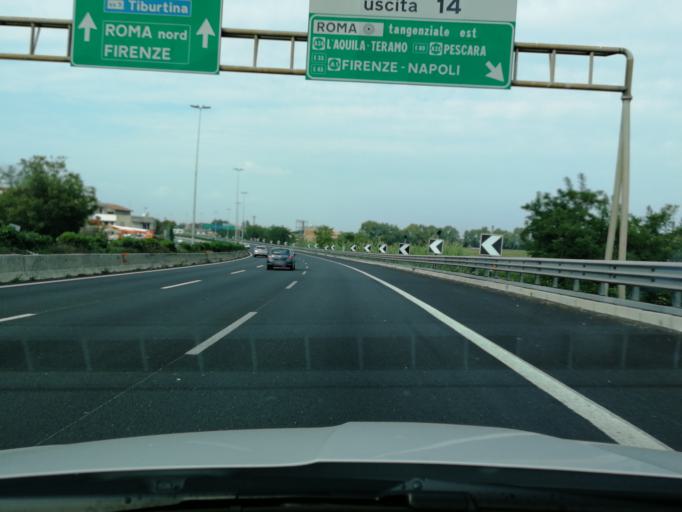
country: IT
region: Latium
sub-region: Citta metropolitana di Roma Capitale
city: Setteville
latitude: 41.9135
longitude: 12.6159
